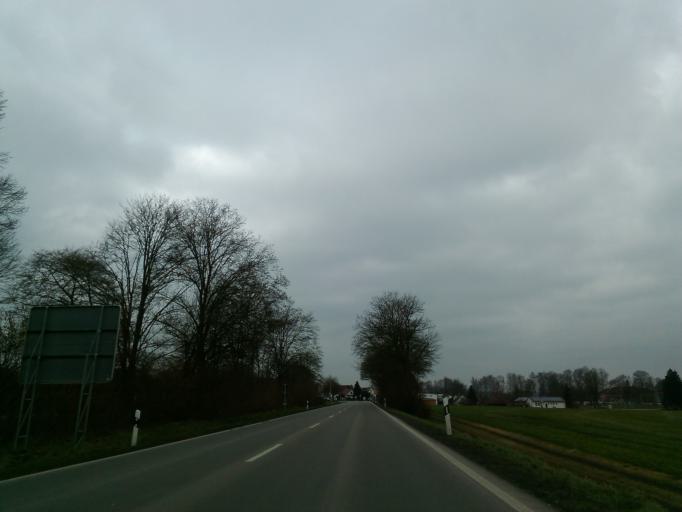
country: DE
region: Bavaria
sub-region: Swabia
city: Ustersbach
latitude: 48.3184
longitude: 10.6519
